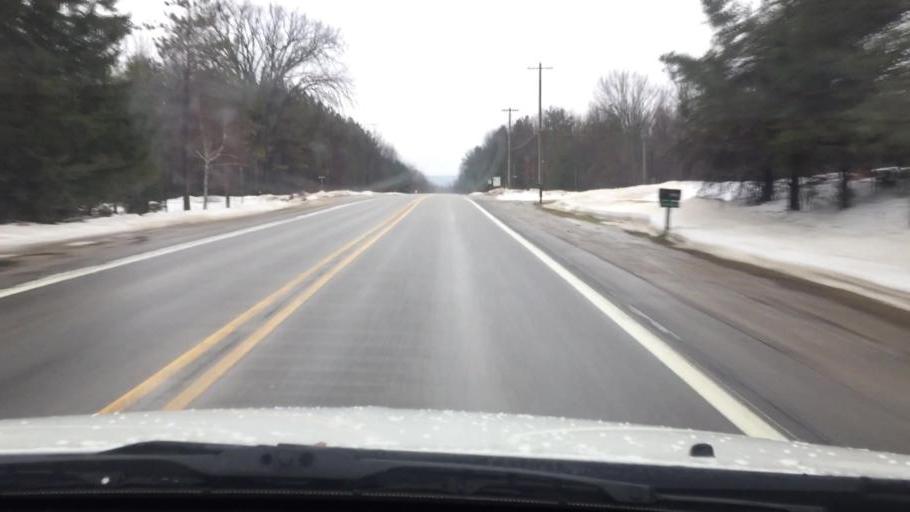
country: US
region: Michigan
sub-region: Charlevoix County
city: Charlevoix
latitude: 45.2660
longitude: -85.2023
